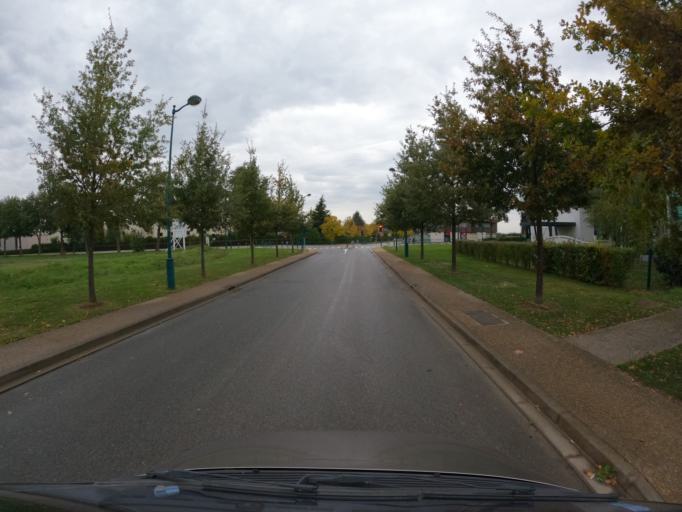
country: FR
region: Ile-de-France
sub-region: Departement de Seine-et-Marne
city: Serris
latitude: 48.8425
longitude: 2.7967
